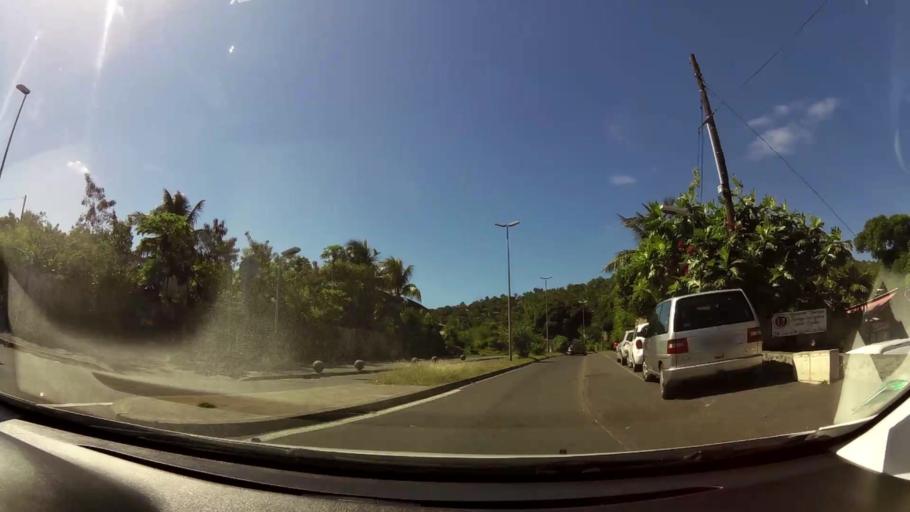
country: YT
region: Pamandzi
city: Pamandzi
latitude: -12.7921
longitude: 45.2803
